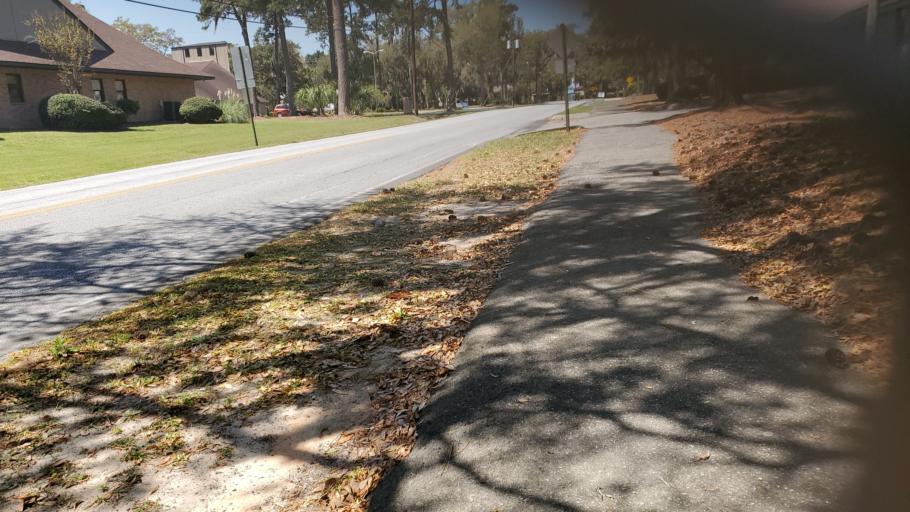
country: US
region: Georgia
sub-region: Chatham County
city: Wilmington Island
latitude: 32.0057
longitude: -80.9877
